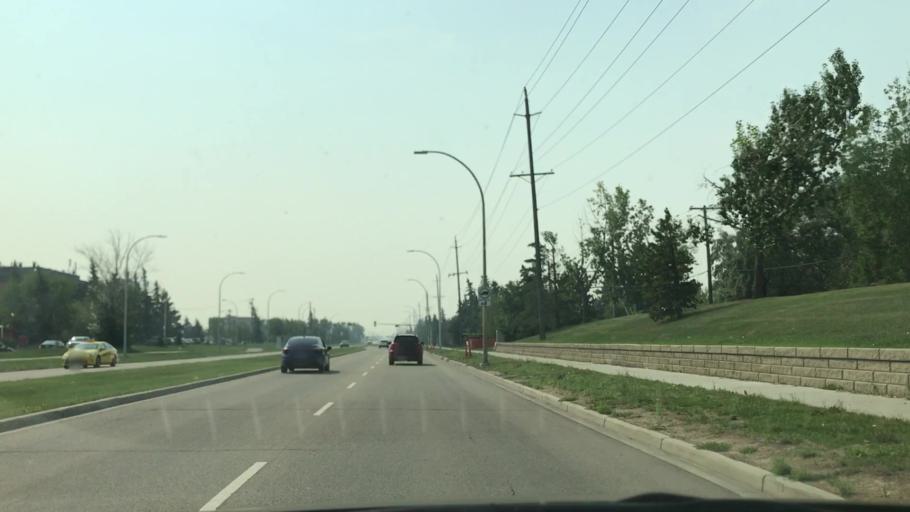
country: CA
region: Alberta
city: Edmonton
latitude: 53.5293
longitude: -113.4191
